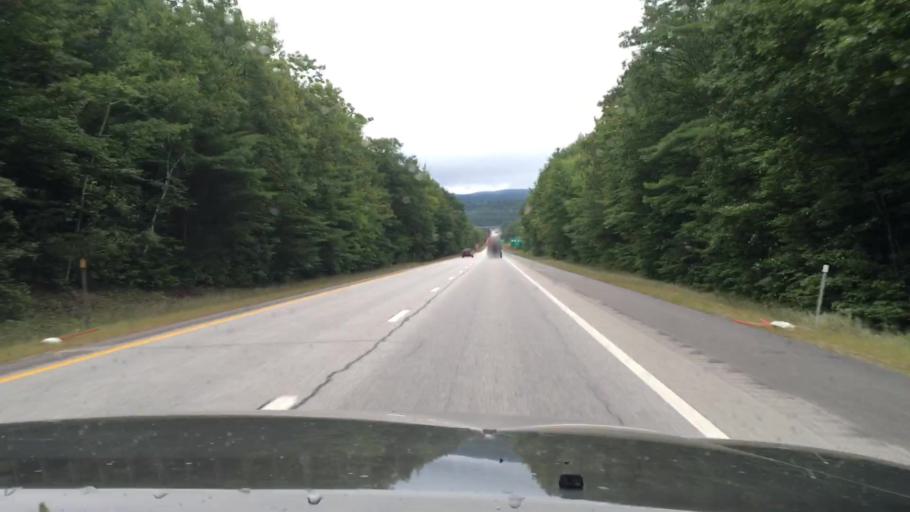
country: US
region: New Hampshire
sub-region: Belknap County
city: Sanbornton
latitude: 43.4740
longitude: -71.5863
